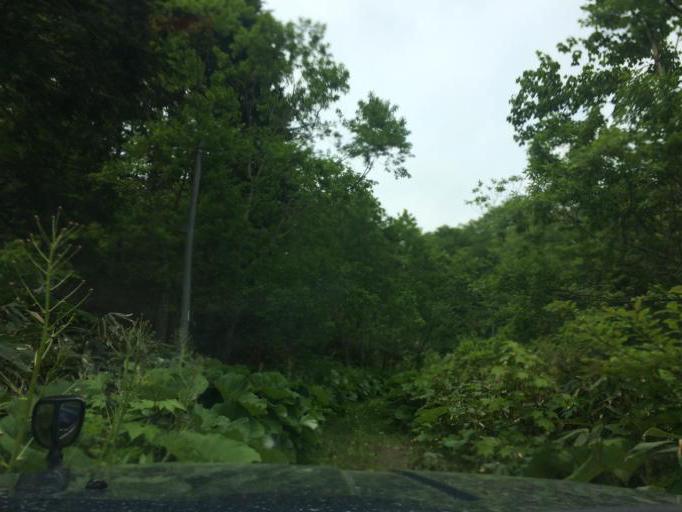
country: JP
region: Hokkaido
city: Niseko Town
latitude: 42.6345
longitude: 140.5717
